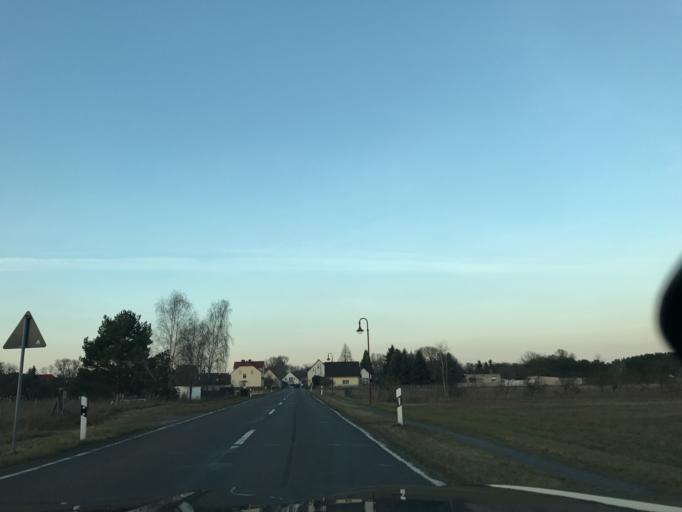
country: DE
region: Brandenburg
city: Wusterwitz
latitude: 52.4373
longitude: 12.4267
